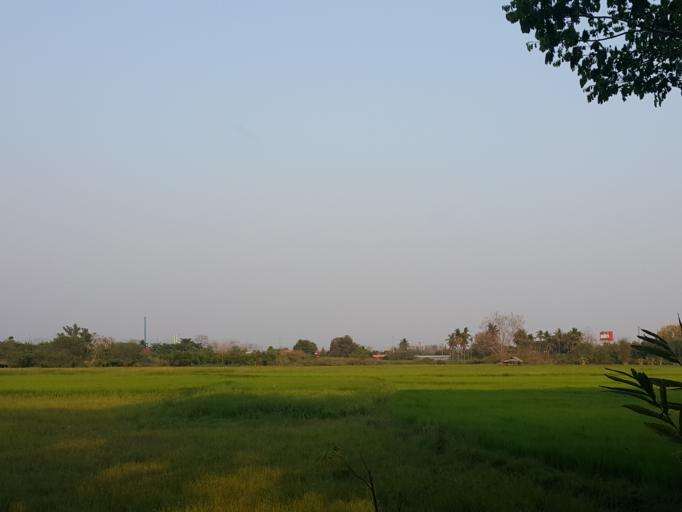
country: TH
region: Chiang Mai
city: San Sai
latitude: 18.8997
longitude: 98.9443
